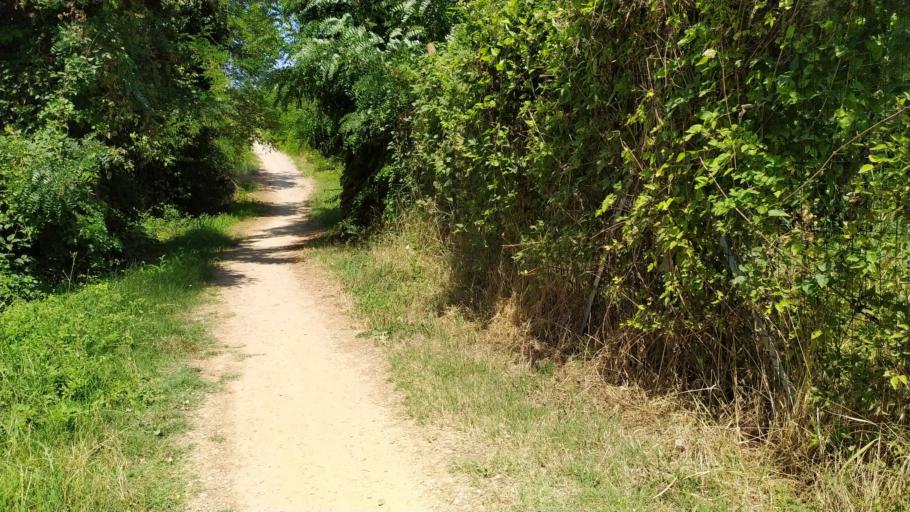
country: IT
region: Emilia-Romagna
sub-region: Forli-Cesena
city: Castrocaro Terme e Terra del Sole
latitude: 44.2041
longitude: 12.0045
